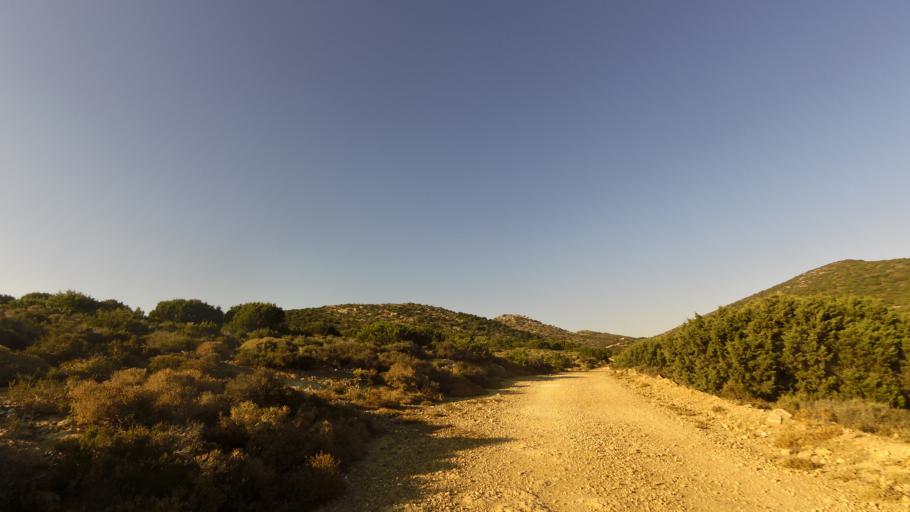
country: GR
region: South Aegean
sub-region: Nomos Kykladon
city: Antiparos
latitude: 36.9919
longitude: 25.0304
